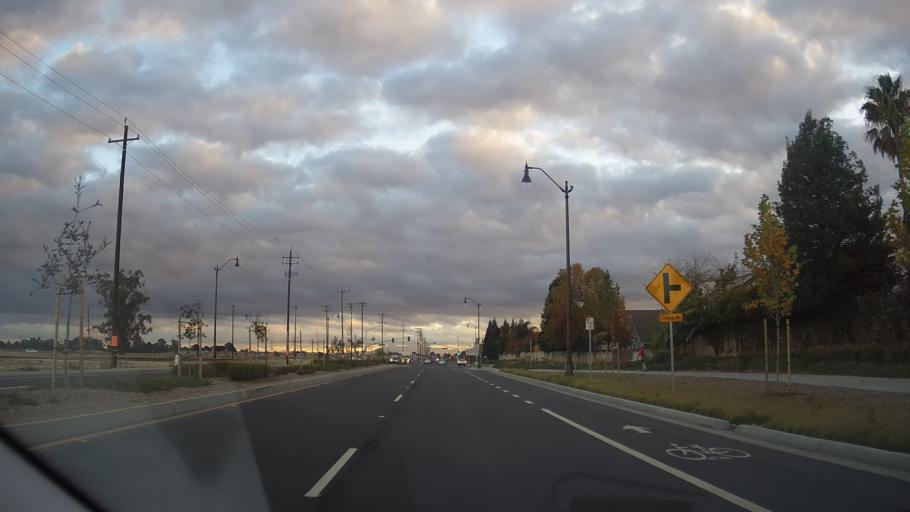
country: US
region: California
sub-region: Solano County
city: Vacaville
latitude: 38.3390
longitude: -121.9339
